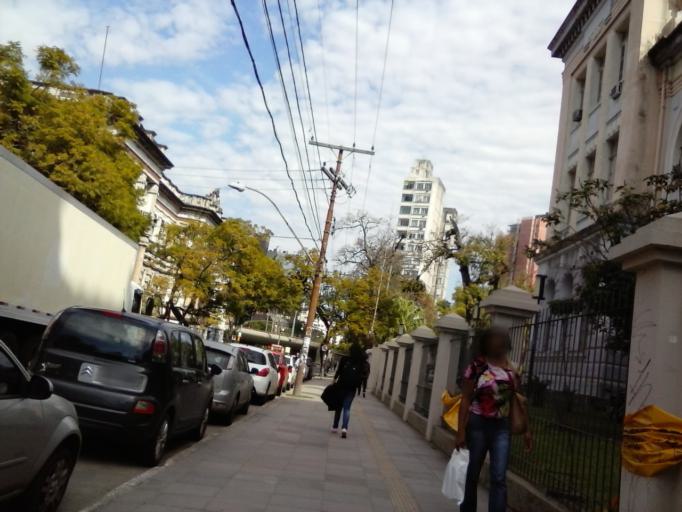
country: BR
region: Rio Grande do Sul
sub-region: Porto Alegre
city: Porto Alegre
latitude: -30.0330
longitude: -51.2211
